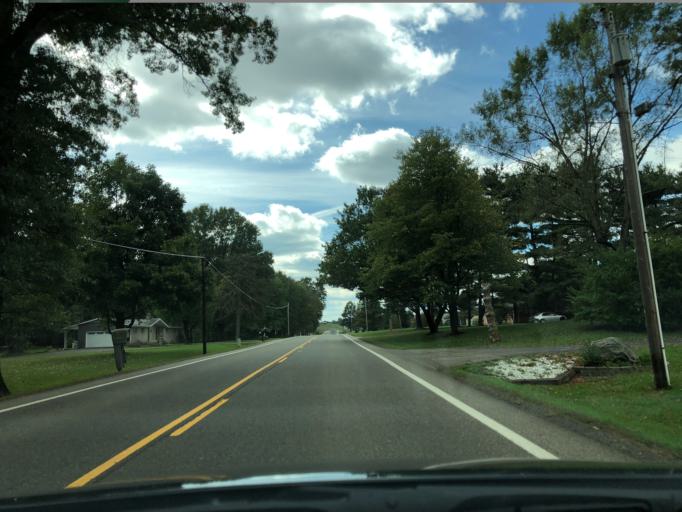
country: US
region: Ohio
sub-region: Stark County
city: Brewster
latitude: 40.6799
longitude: -81.6086
